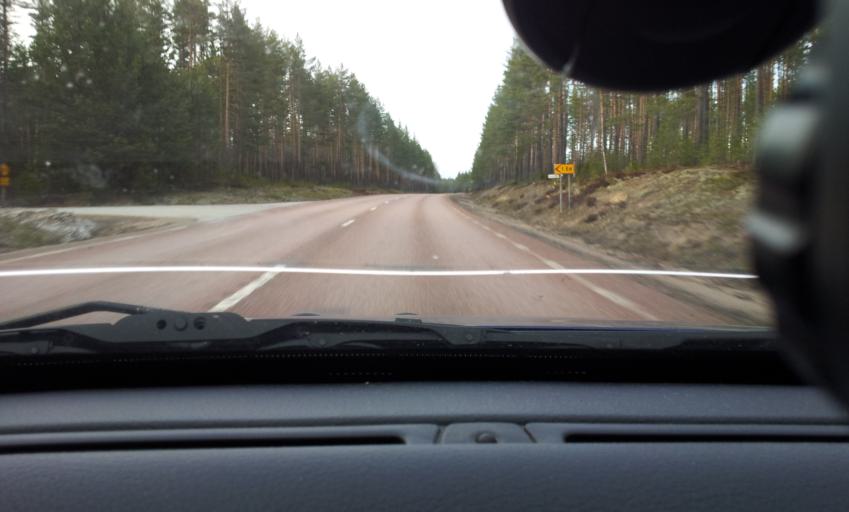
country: SE
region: Gaevleborg
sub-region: Ljusdals Kommun
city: Farila
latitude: 61.8422
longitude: 15.7506
